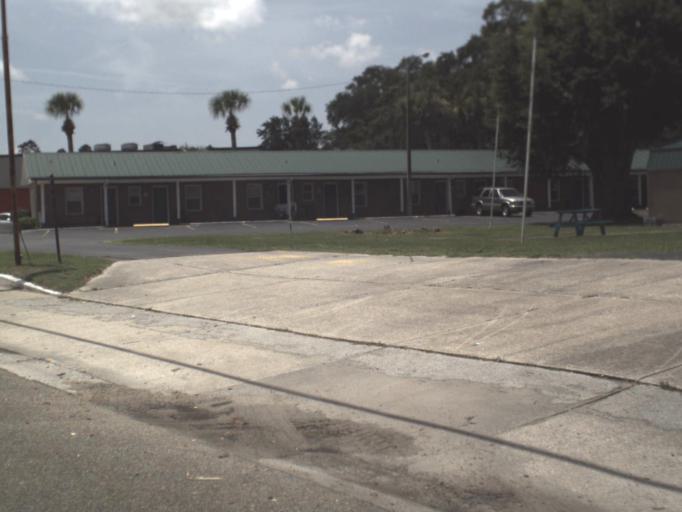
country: US
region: Florida
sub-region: Taylor County
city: Perry
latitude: 30.0944
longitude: -83.5794
